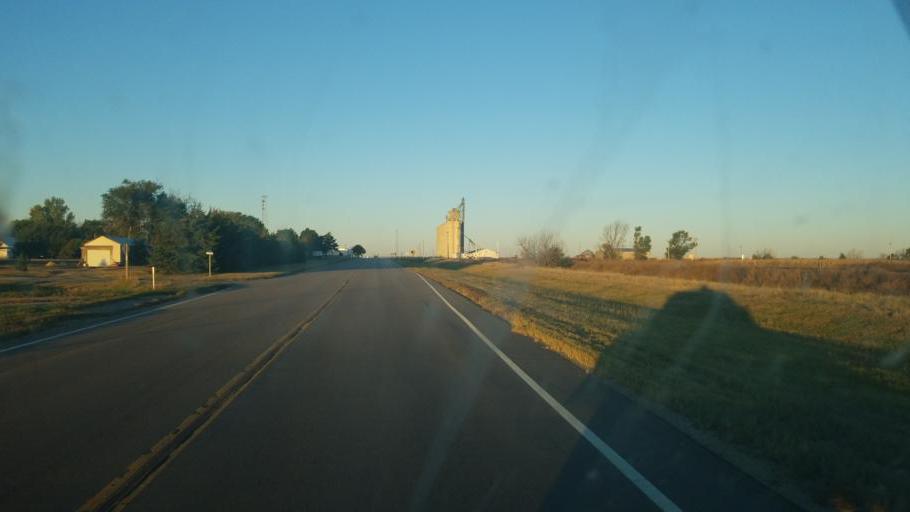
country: US
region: Kansas
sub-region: Wallace County
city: Sharon Springs
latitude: 38.8697
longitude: -101.9604
